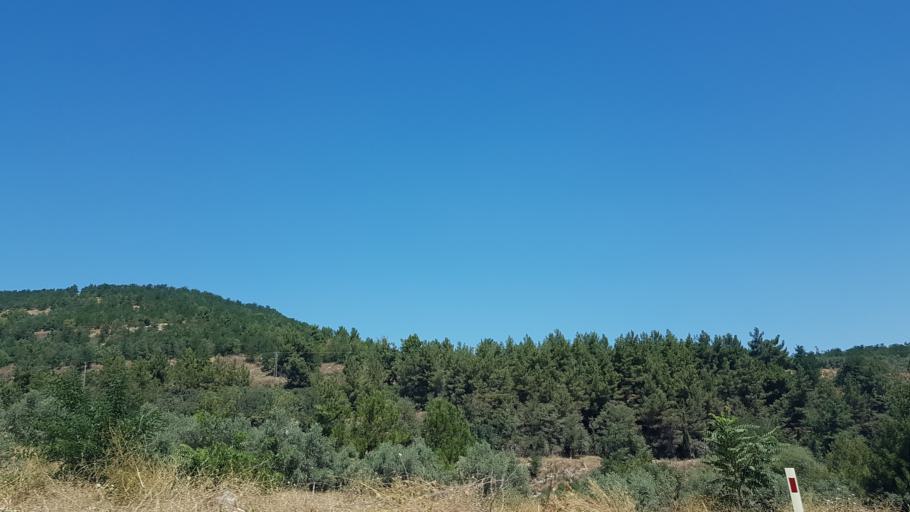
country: TR
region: Mugla
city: Yatagan
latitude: 37.3190
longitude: 28.0781
